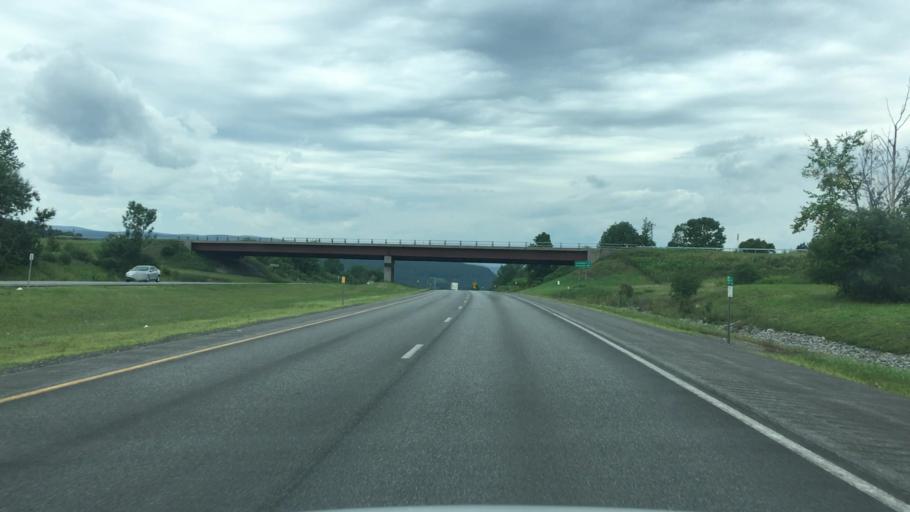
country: US
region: New York
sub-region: Schoharie County
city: Schoharie
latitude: 42.7144
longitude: -74.2745
